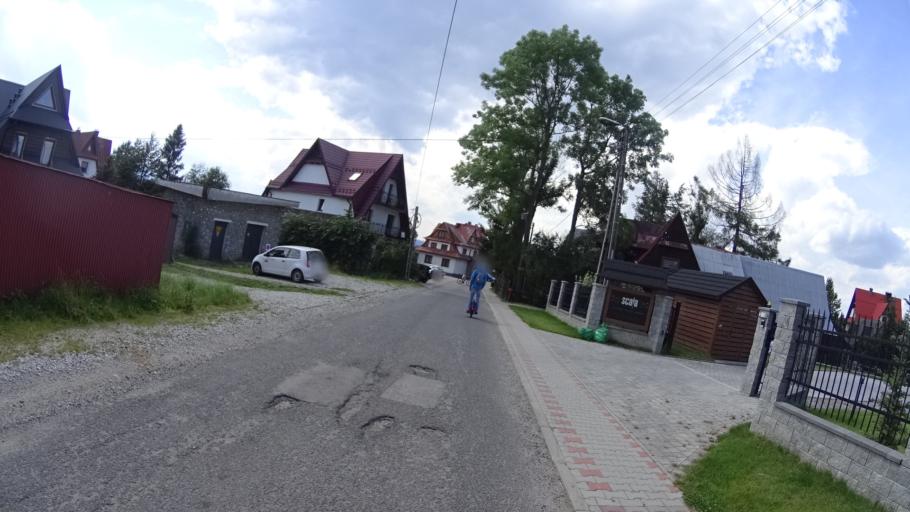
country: PL
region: Lesser Poland Voivodeship
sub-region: Powiat tatrzanski
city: Bukowina Tatrzanska
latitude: 49.3330
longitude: 20.0902
